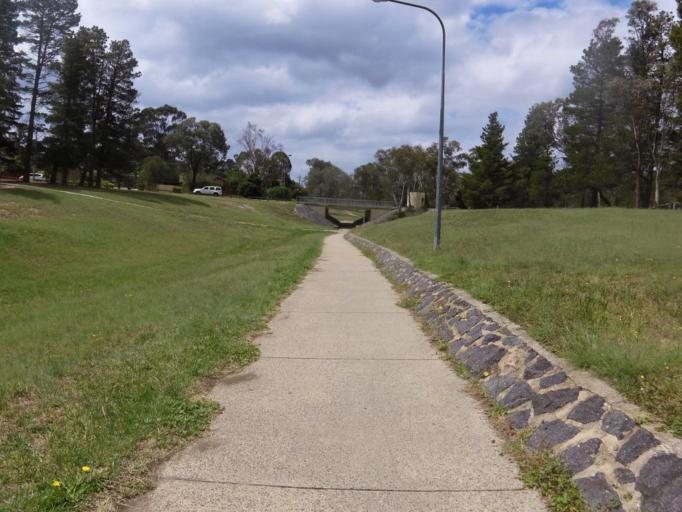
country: AU
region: Australian Capital Territory
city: Macarthur
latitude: -35.4098
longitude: 149.1274
